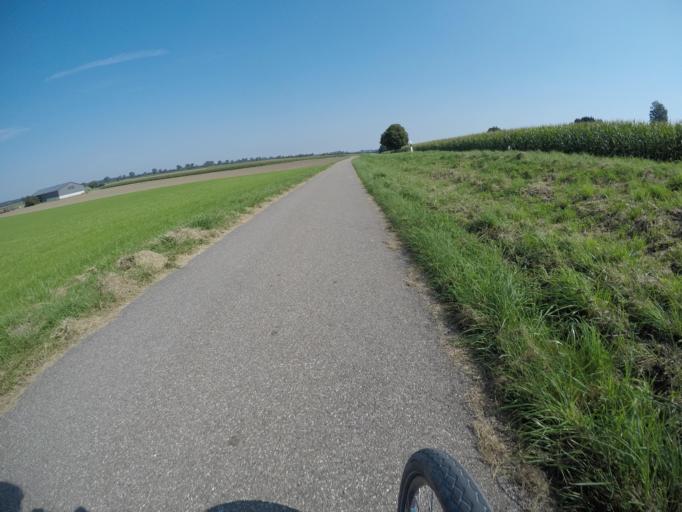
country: DE
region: Bavaria
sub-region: Swabia
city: Holzheim
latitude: 48.5160
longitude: 10.5362
